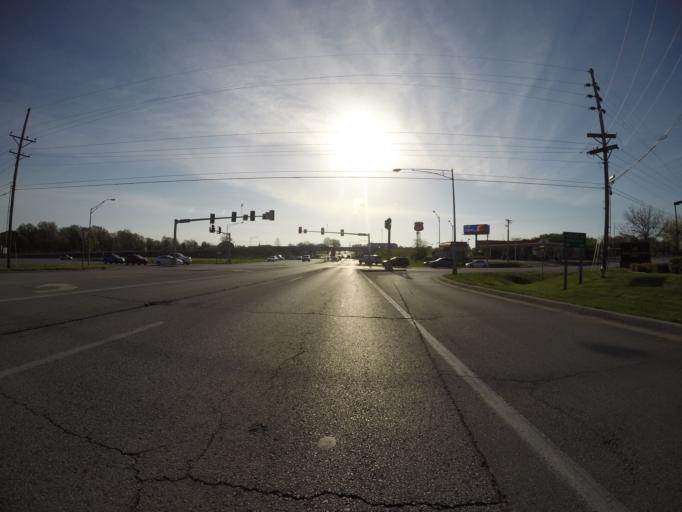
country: US
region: Missouri
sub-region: Jackson County
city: Lees Summit
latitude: 38.9112
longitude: -94.3963
